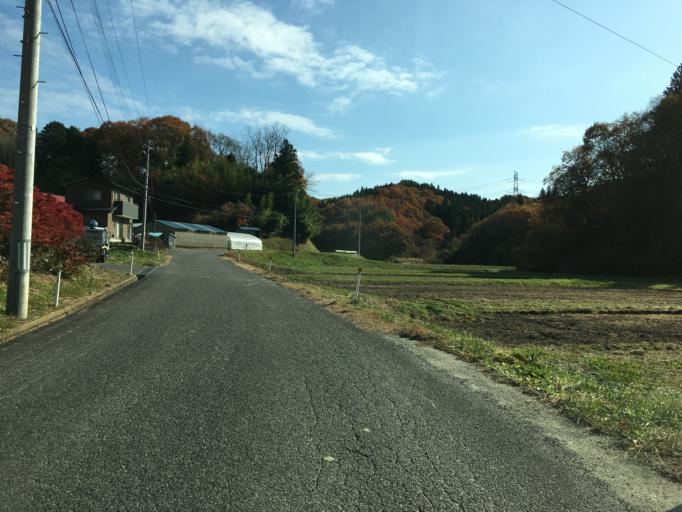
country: JP
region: Fukushima
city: Ishikawa
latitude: 37.1744
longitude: 140.5546
